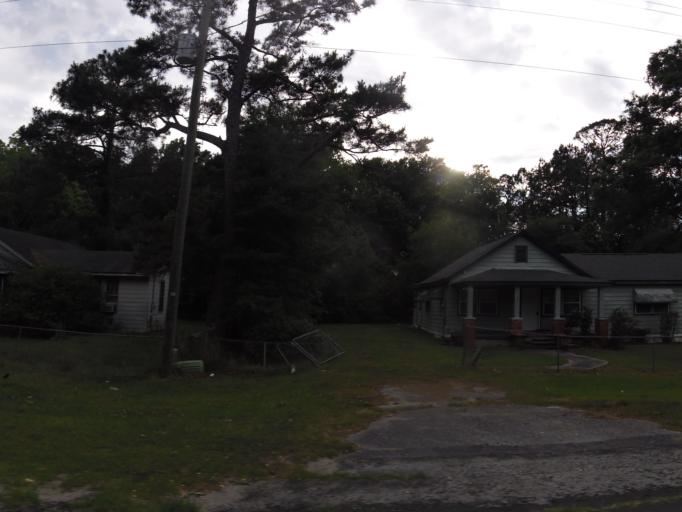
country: US
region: South Carolina
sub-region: Jasper County
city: Hardeeville
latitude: 32.2954
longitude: -81.0860
